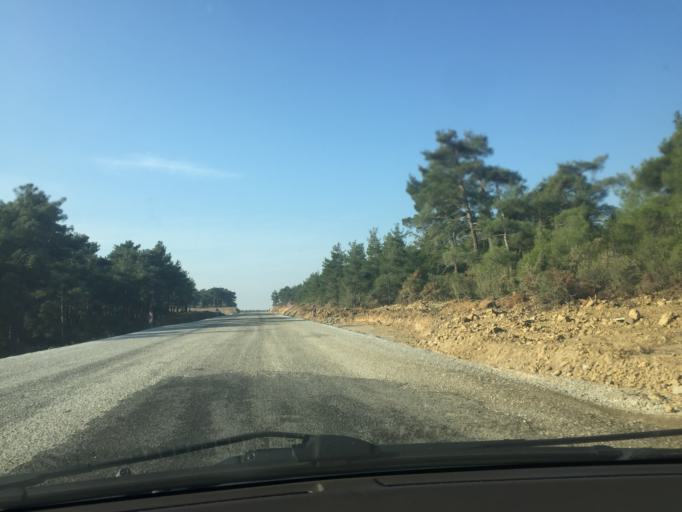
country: TR
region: Canakkale
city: Yigitler
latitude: 39.8925
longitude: 26.7199
